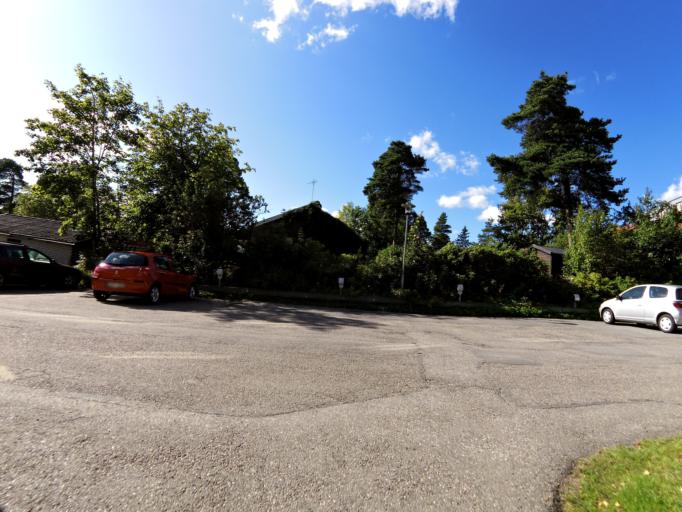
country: SE
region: Gaevleborg
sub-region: Gavle Kommun
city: Gavle
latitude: 60.6951
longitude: 17.1489
